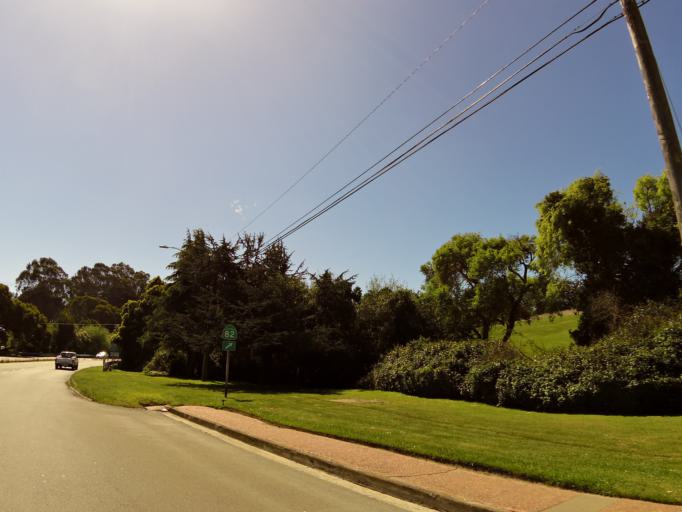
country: US
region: California
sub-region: San Mateo County
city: Colma
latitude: 37.6730
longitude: -122.4543
